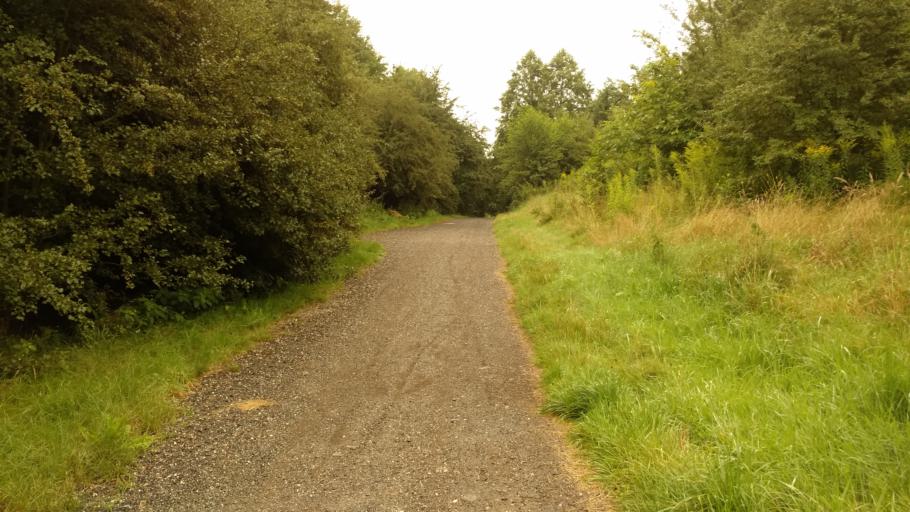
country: PL
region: Lesser Poland Voivodeship
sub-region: Powiat krakowski
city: Michalowice
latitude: 50.1323
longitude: 19.9756
